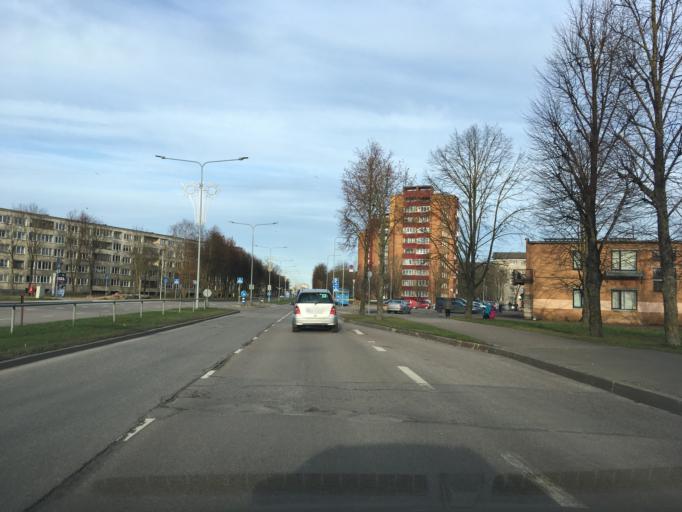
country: EE
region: Ida-Virumaa
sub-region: Narva linn
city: Narva
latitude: 59.3657
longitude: 28.1878
